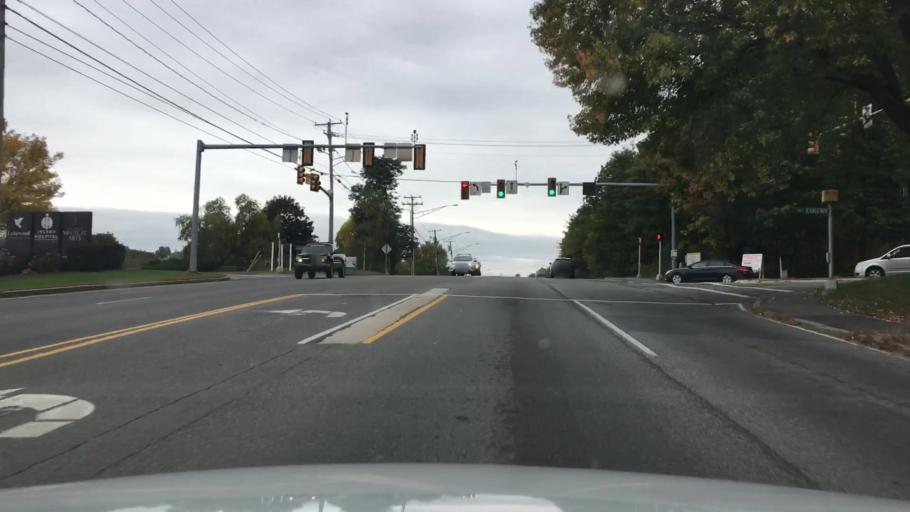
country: US
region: Maine
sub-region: Kennebec County
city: Waterville
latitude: 44.5427
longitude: -69.6610
